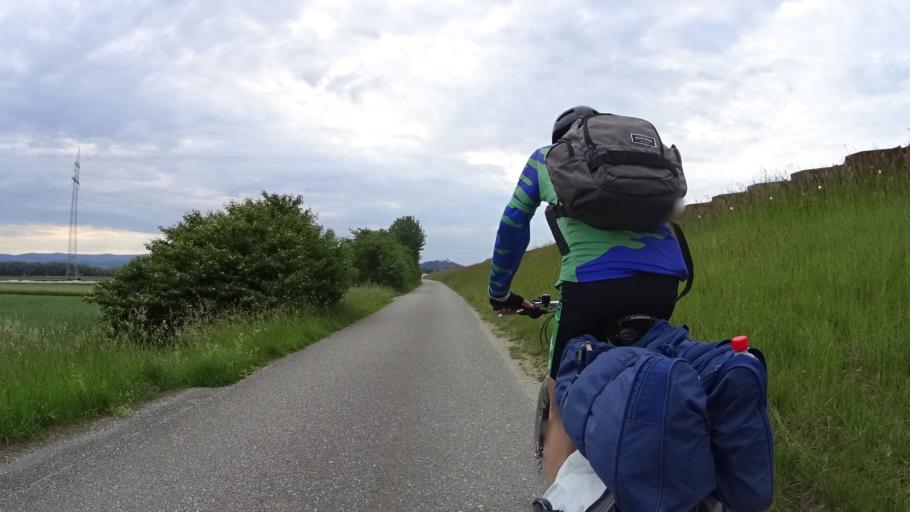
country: DE
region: Bavaria
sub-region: Lower Bavaria
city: Parkstetten
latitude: 48.9096
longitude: 12.6361
